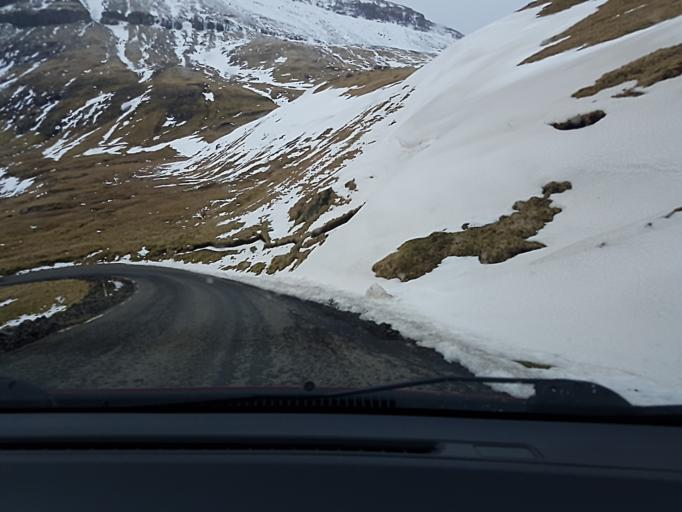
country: FO
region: Streymoy
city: Kollafjordhur
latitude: 62.0539
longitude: -6.9196
